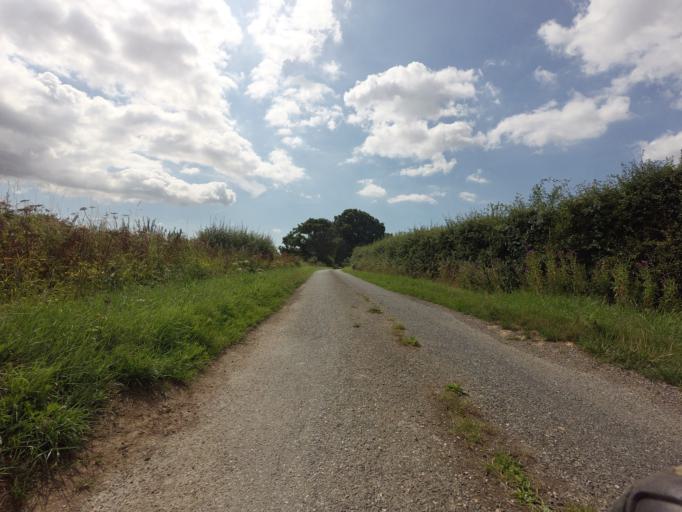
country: GB
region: England
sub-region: Kent
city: Stone
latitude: 51.0503
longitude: 0.7721
